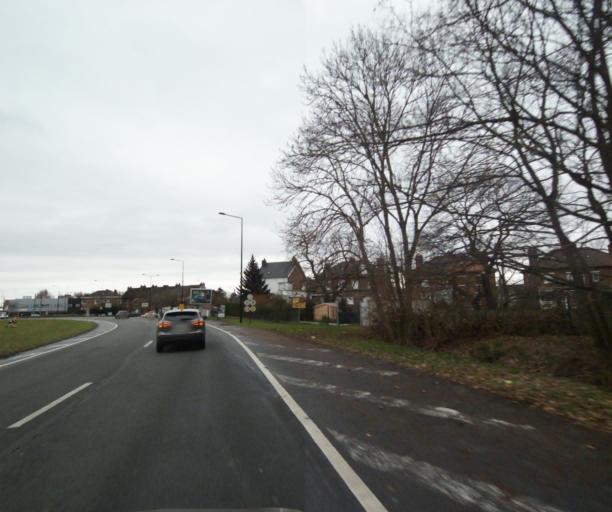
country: FR
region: Nord-Pas-de-Calais
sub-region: Departement du Nord
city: La Sentinelle
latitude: 50.3559
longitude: 3.4921
